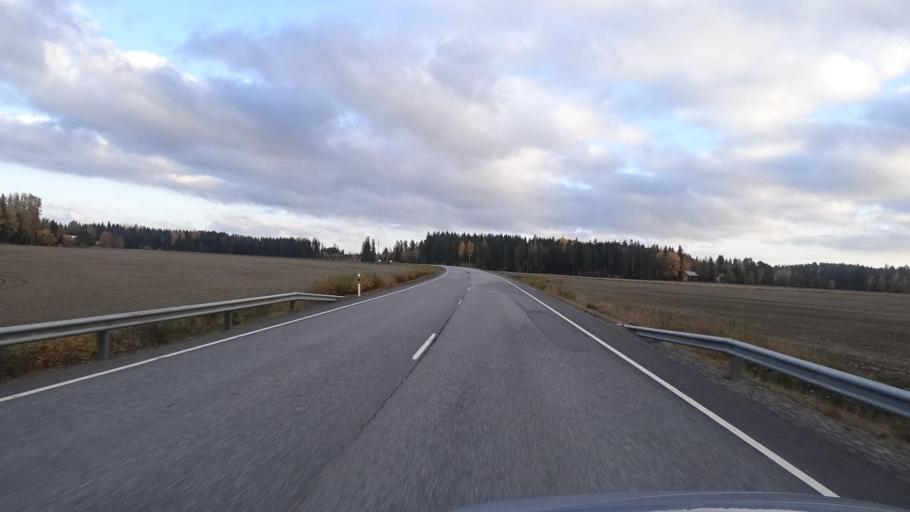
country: FI
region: Varsinais-Suomi
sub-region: Loimaa
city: Alastaro
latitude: 60.8835
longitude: 22.9767
